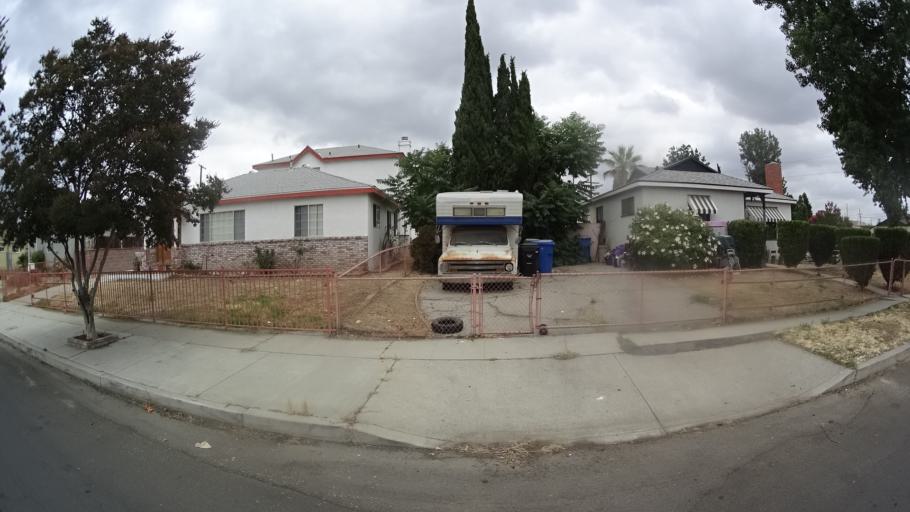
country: US
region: California
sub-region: Los Angeles County
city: San Fernando
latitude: 34.2515
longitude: -118.4455
